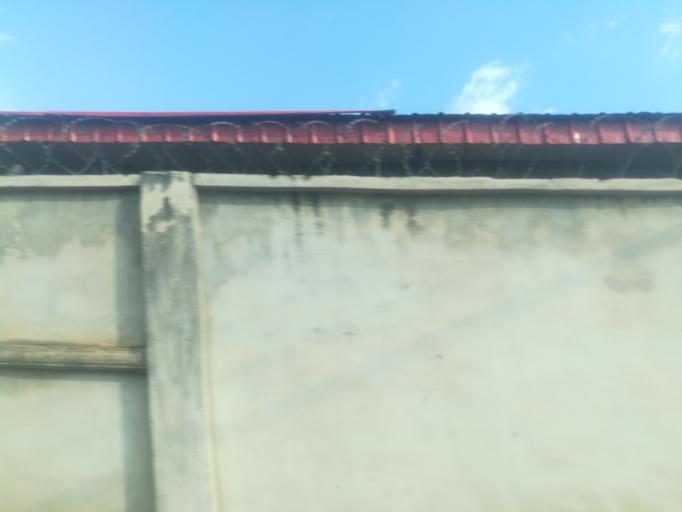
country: NG
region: Oyo
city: Ibadan
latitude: 7.4205
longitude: 3.8433
